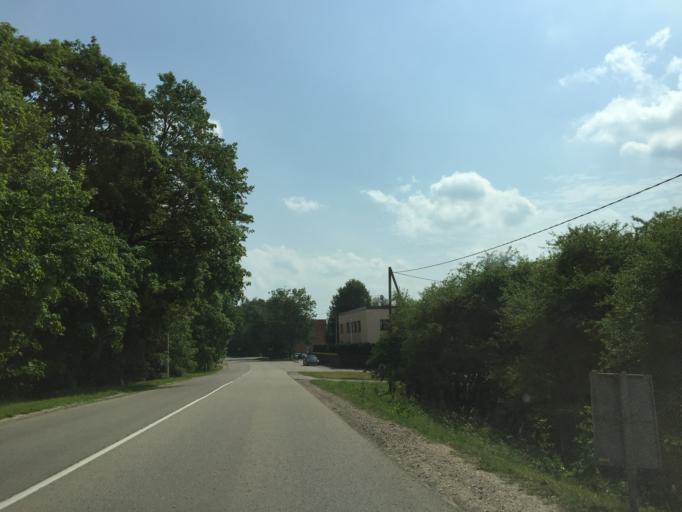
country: LV
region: Jelgava
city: Jelgava
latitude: 56.6873
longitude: 23.7197
